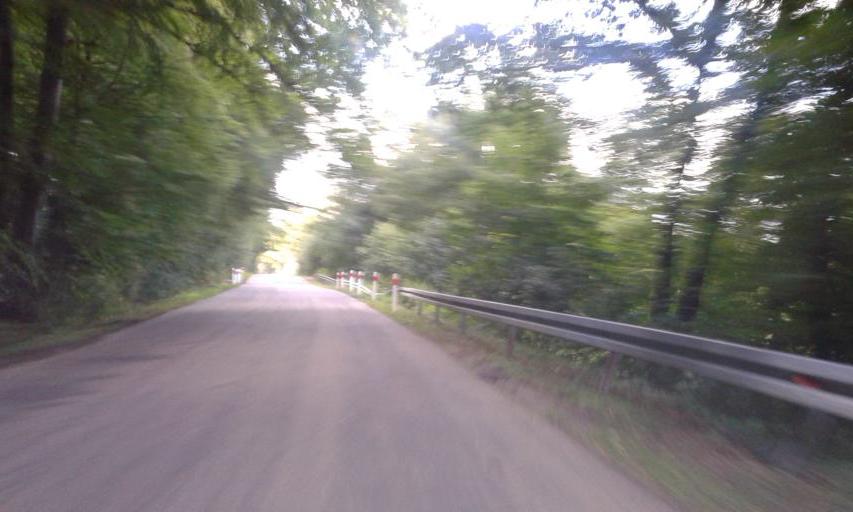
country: PL
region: West Pomeranian Voivodeship
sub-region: Powiat szczecinecki
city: Barwice
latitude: 53.6940
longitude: 16.3481
